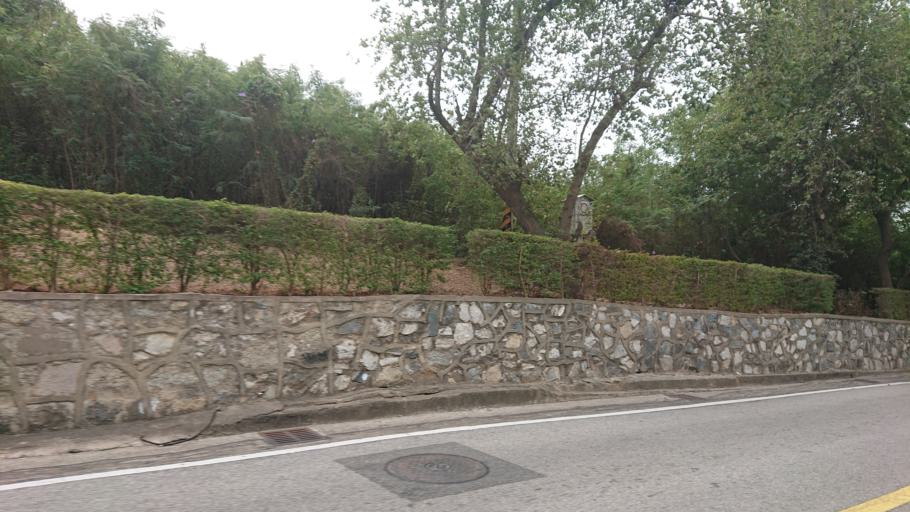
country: TW
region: Fukien
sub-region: Kinmen
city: Jincheng
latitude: 24.4273
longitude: 118.2605
